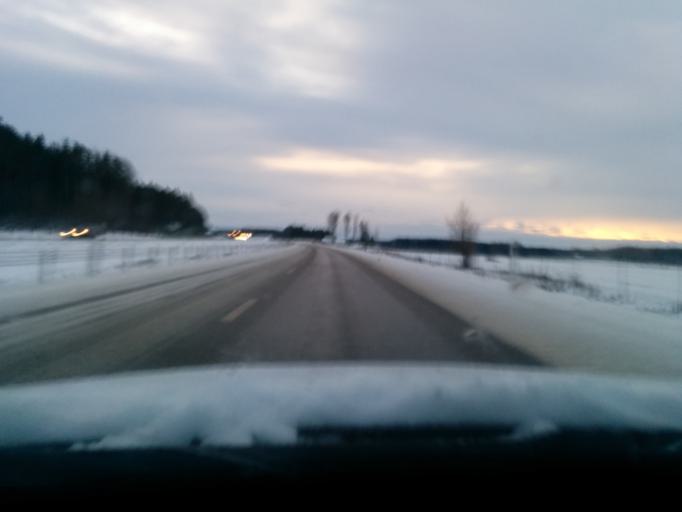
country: SE
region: Uppsala
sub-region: Osthammars Kommun
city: Bjorklinge
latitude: 60.0968
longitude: 17.5685
